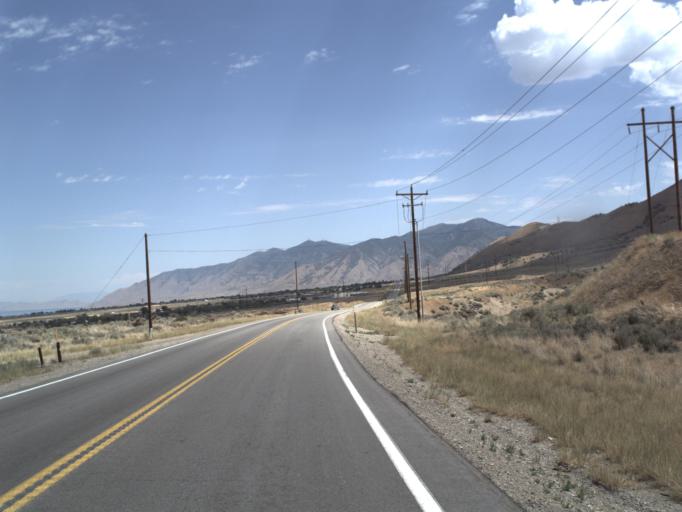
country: US
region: Utah
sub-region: Tooele County
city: Tooele
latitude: 40.4756
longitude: -112.3478
